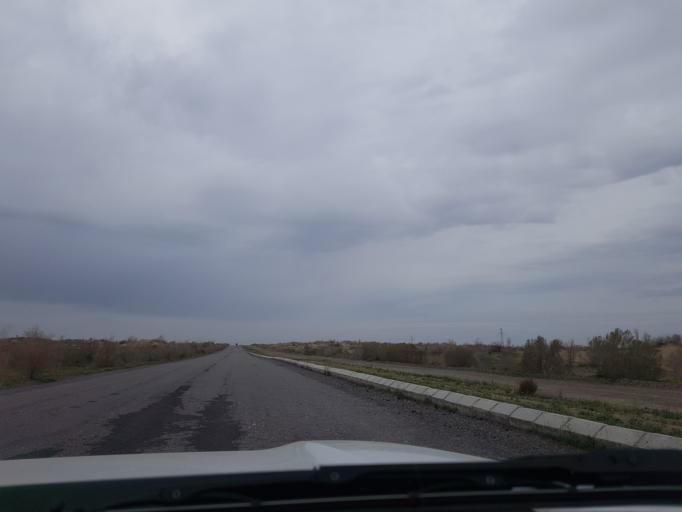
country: TM
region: Lebap
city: Turkmenabat
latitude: 38.9249
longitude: 63.4695
